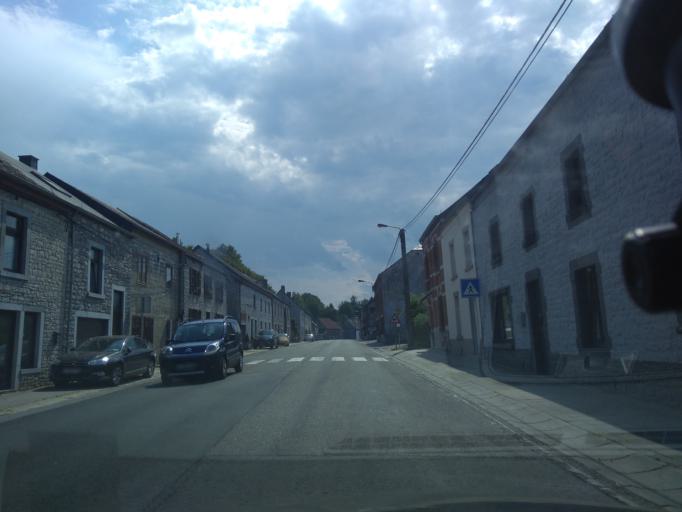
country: BE
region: Wallonia
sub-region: Province de Namur
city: Dinant
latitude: 50.2048
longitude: 4.8960
